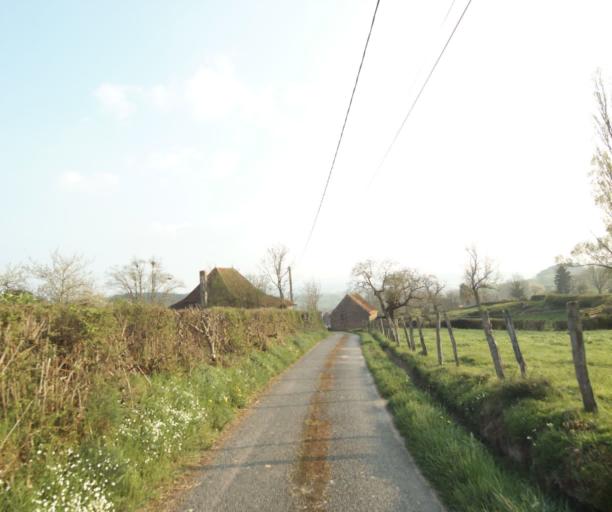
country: FR
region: Bourgogne
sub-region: Departement de Saone-et-Loire
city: Matour
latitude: 46.4324
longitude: 4.4601
